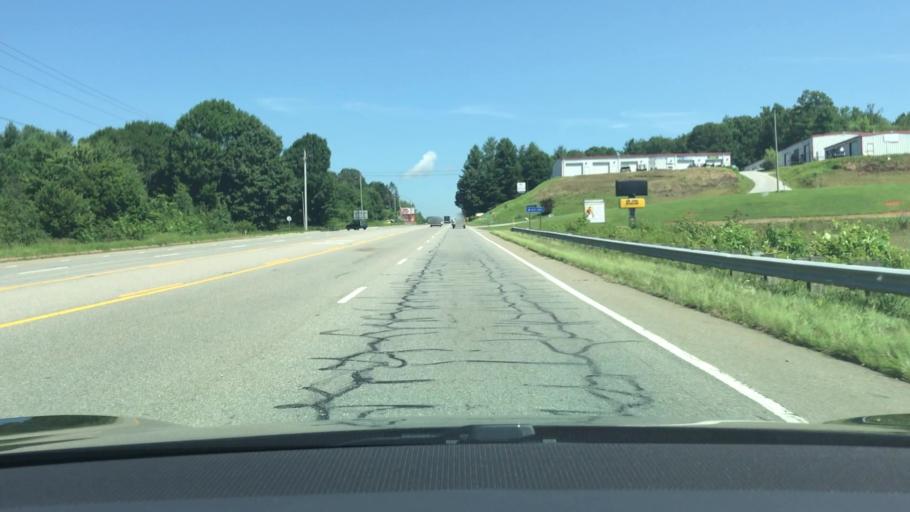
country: US
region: North Carolina
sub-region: Macon County
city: Franklin
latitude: 35.1125
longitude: -83.3893
